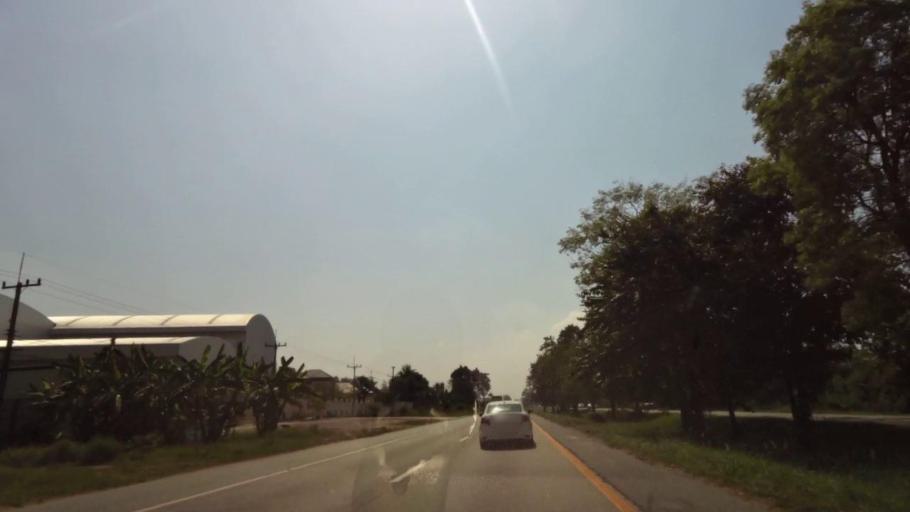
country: TH
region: Phichit
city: Wachira Barami
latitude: 16.6022
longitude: 100.1480
